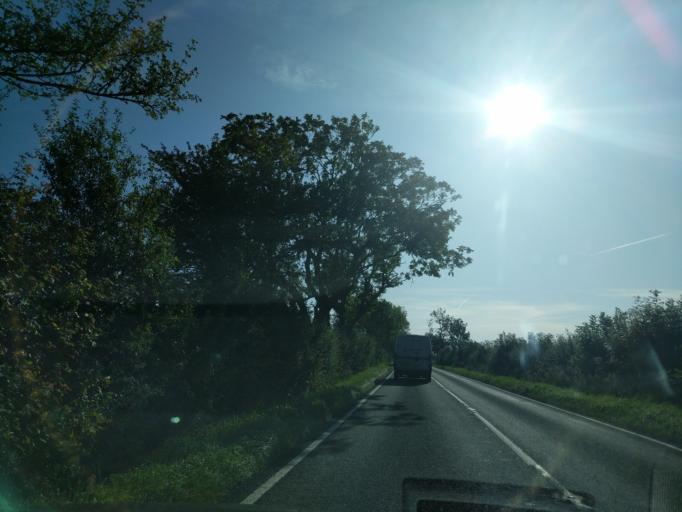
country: GB
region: England
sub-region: District of Rutland
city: Clipsham
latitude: 52.8076
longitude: -0.4990
